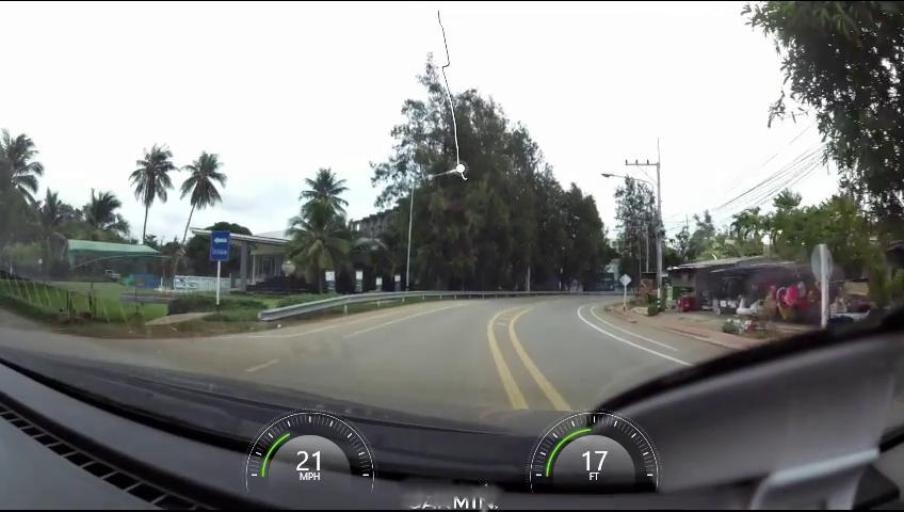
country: TH
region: Prachuap Khiri Khan
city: Hua Hin
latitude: 12.4665
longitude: 99.9734
